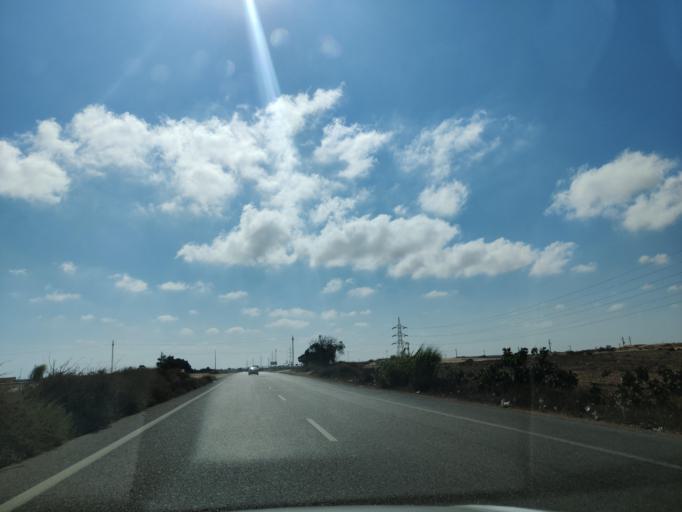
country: EG
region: Muhafazat Matruh
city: Al `Alamayn
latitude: 31.0541
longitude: 28.2885
